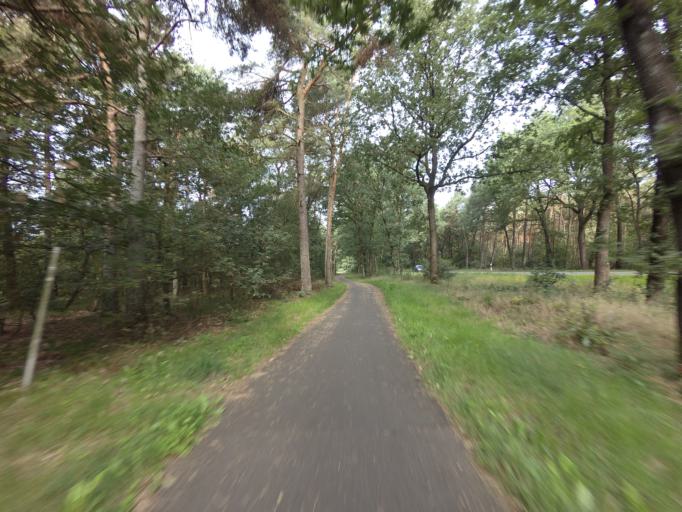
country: DE
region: Lower Saxony
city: Itterbeck
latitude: 52.5099
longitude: 6.7851
